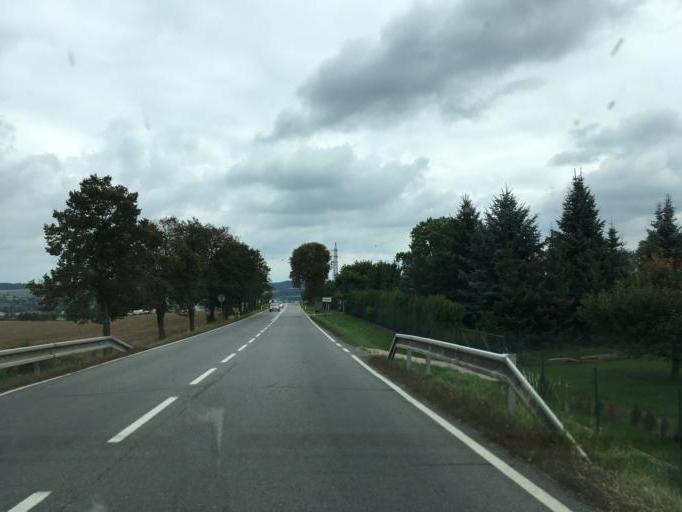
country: CZ
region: Vysocina
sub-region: Okres Pelhrimov
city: Pelhrimov
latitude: 49.4431
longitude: 15.2013
